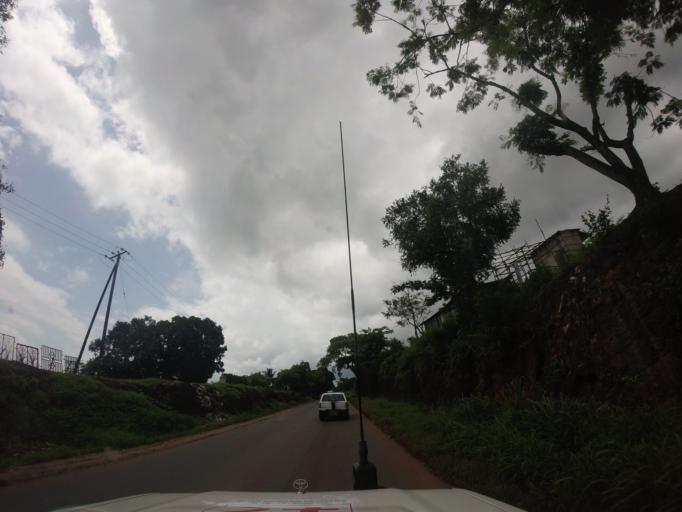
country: SL
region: Western Area
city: Waterloo
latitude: 8.3675
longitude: -13.0904
